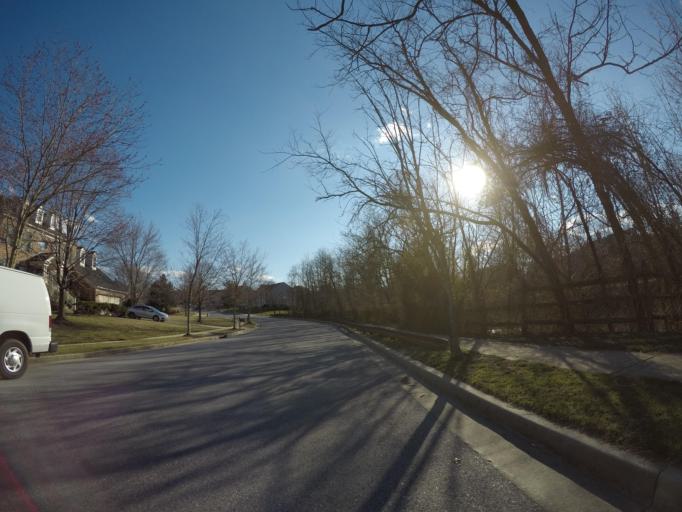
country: US
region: Maryland
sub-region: Howard County
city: Ellicott City
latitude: 39.2553
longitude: -76.8040
